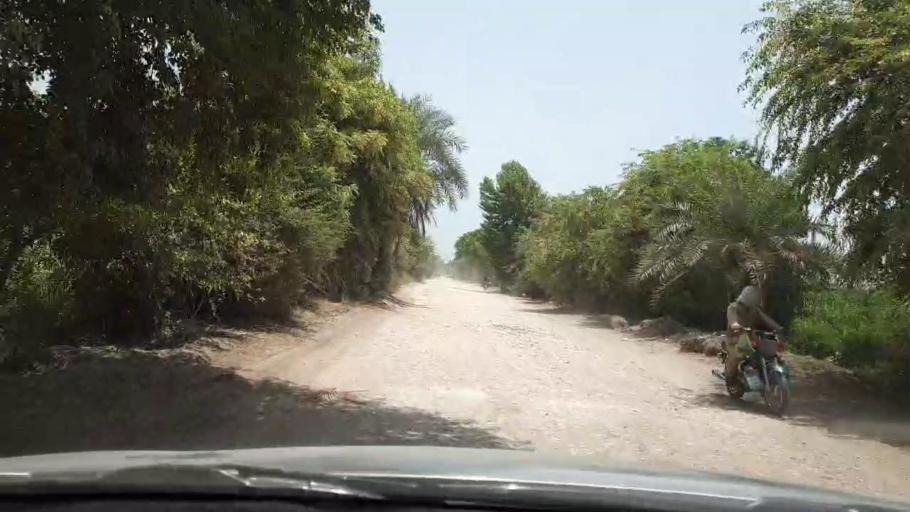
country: PK
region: Sindh
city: Pano Aqil
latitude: 27.8596
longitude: 69.0905
